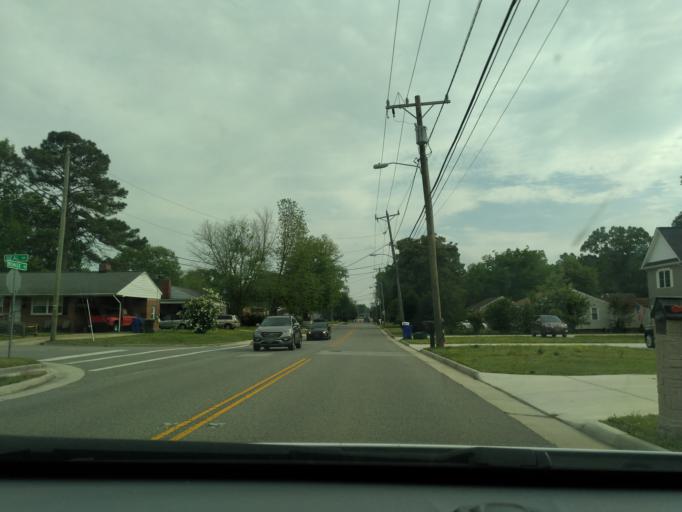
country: US
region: Virginia
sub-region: York County
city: Yorktown
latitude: 37.1553
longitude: -76.5271
